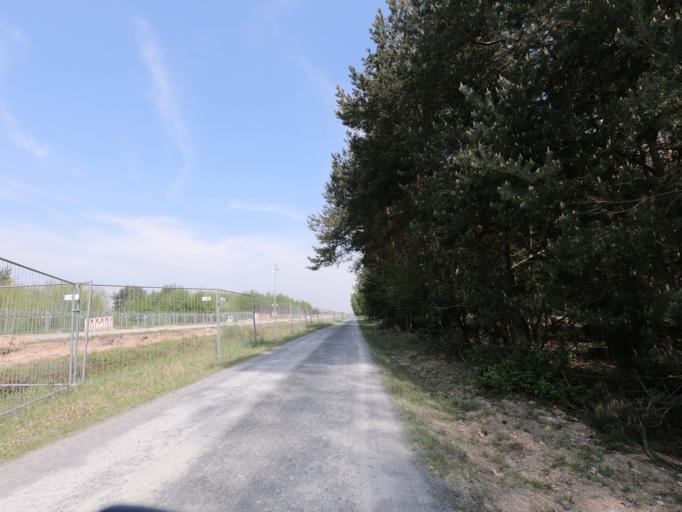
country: DE
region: Hesse
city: Kelsterbach
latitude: 50.0076
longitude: 8.5303
